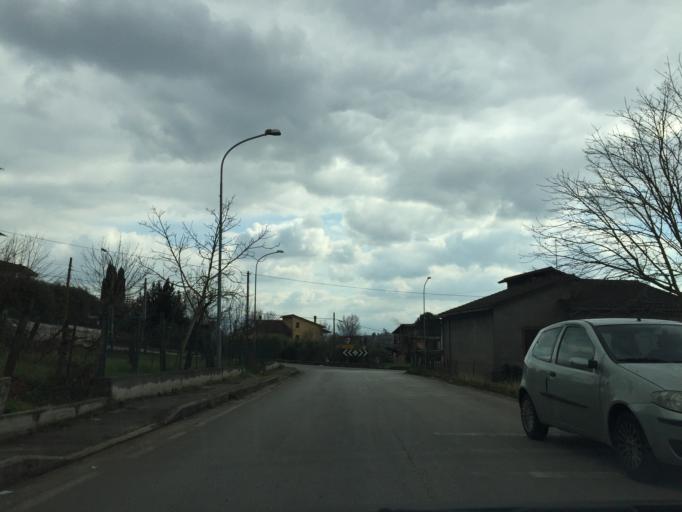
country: IT
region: Latium
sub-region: Provincia di Frosinone
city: Villa Santa Lucia
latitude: 41.4906
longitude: 13.7836
